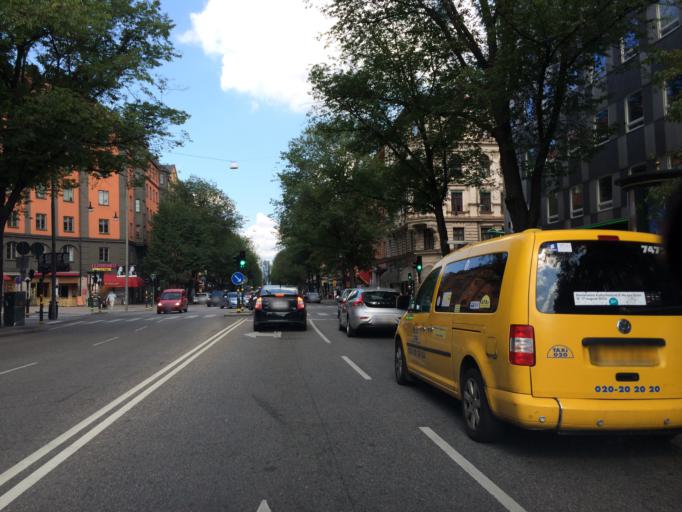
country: SE
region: Stockholm
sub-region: Stockholms Kommun
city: Stockholm
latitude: 59.3391
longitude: 18.0602
